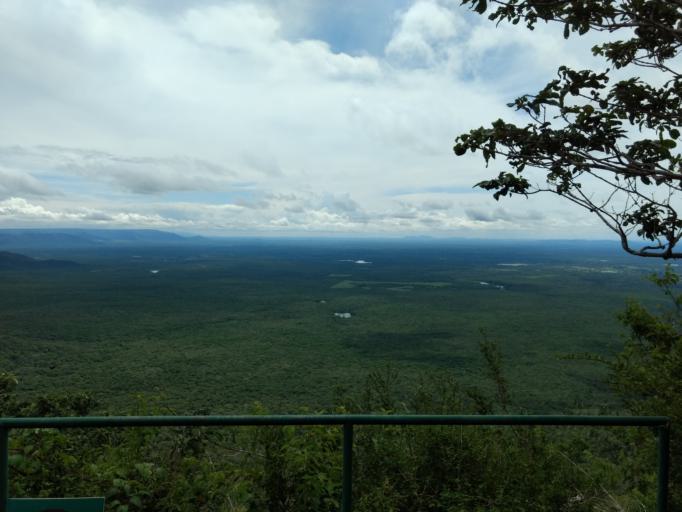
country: BR
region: Ceara
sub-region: Crateus
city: Crateus
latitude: -5.1631
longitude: -40.8770
